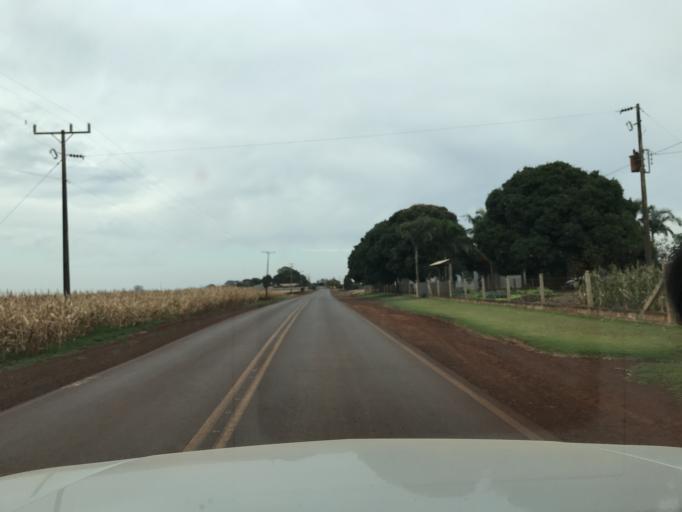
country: BR
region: Parana
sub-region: Palotina
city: Palotina
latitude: -24.4188
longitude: -53.8766
